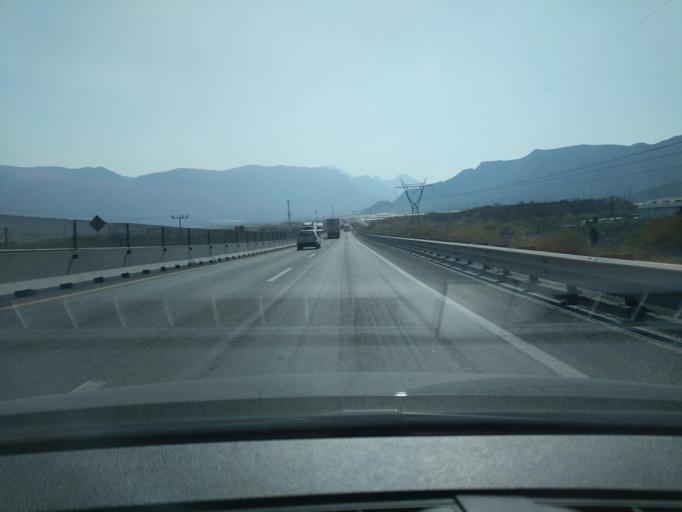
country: MX
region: Nuevo Leon
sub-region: Garcia
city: Los Parques
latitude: 25.7430
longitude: -100.5139
